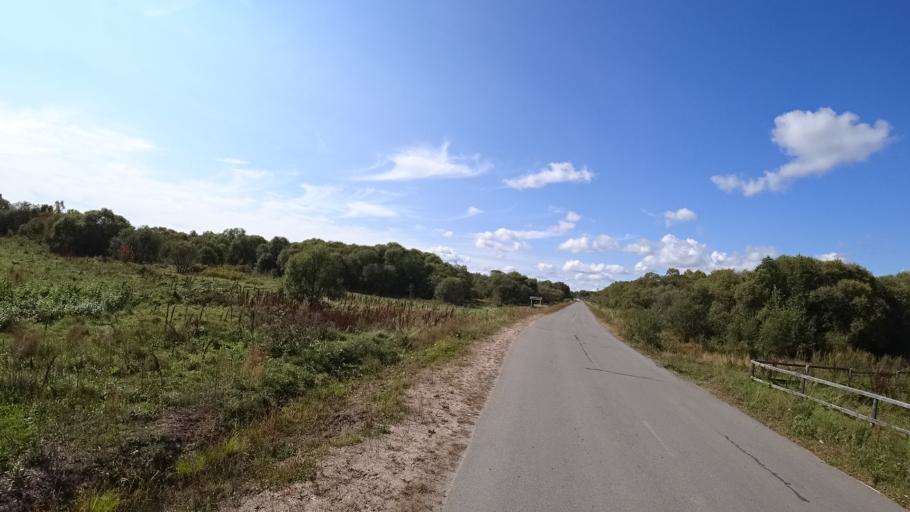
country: RU
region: Amur
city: Arkhara
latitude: 49.4039
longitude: 130.1319
